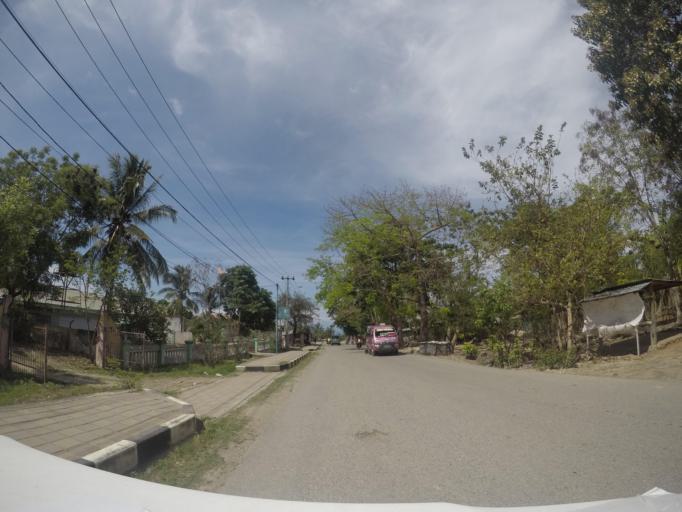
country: TL
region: Baucau
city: Baucau
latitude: -8.4695
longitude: 126.4590
